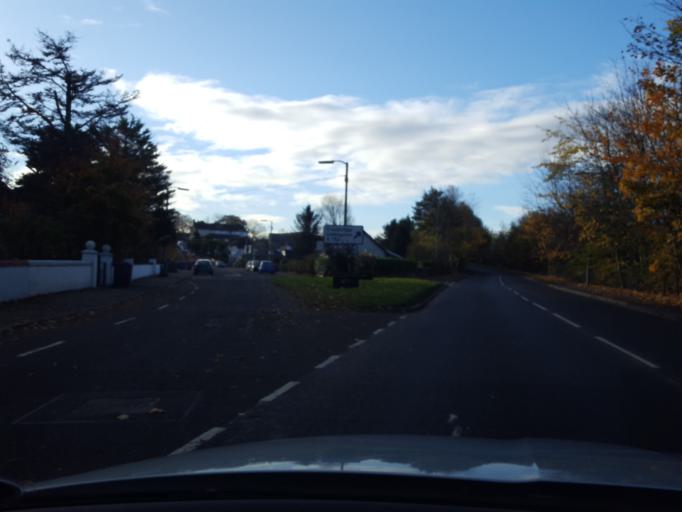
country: GB
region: Scotland
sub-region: North Lanarkshire
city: Chryston
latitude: 55.8910
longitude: -4.0829
